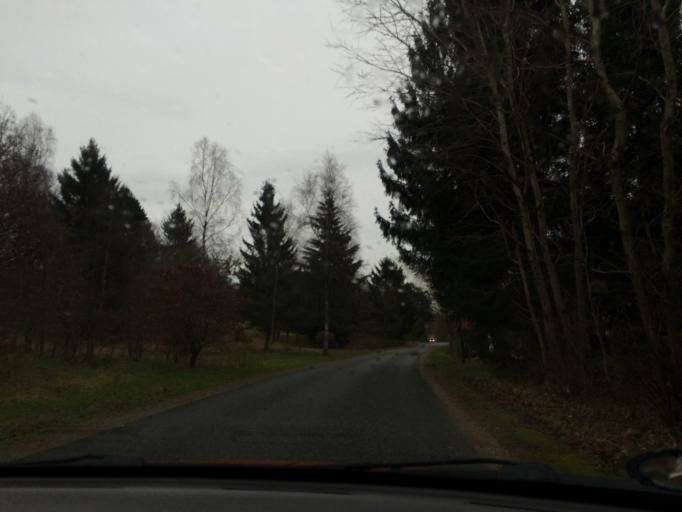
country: DK
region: Central Jutland
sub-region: Silkeborg Kommune
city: Virklund
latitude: 56.0362
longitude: 9.4857
